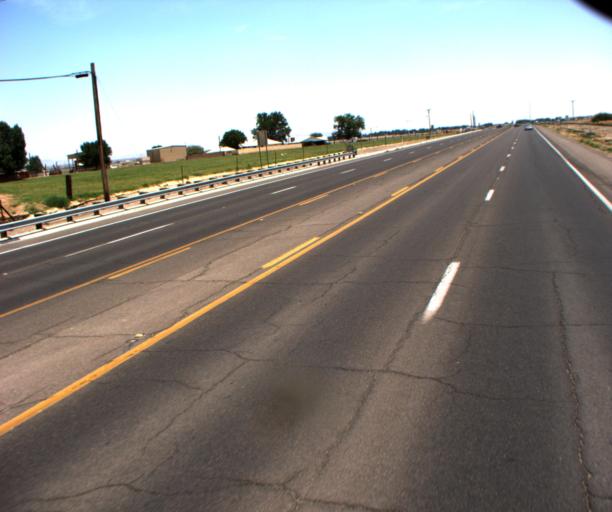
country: US
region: Arizona
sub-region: Graham County
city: Pima
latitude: 32.8892
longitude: -109.8165
